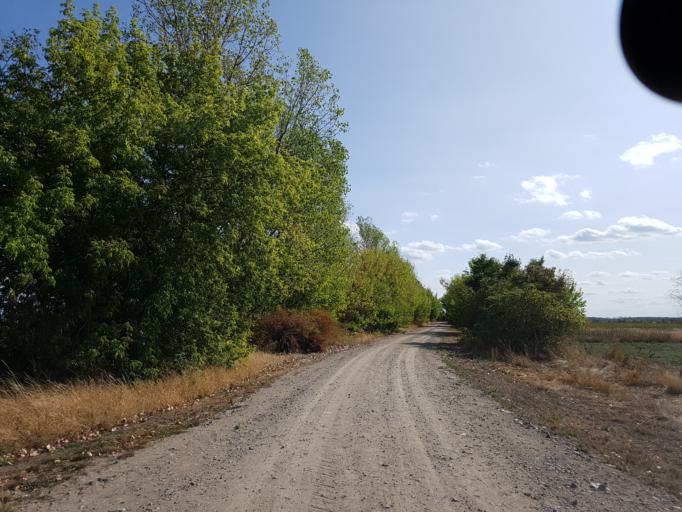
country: DE
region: Brandenburg
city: Treuenbrietzen
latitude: 51.9989
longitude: 12.8575
